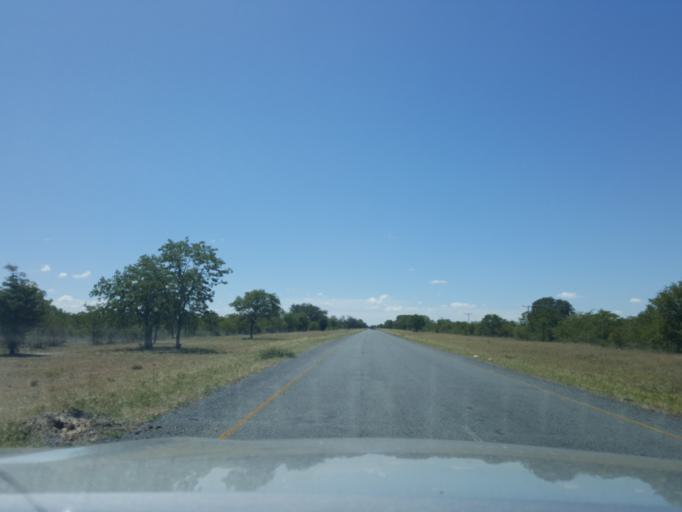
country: BW
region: Central
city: Gweta
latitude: -20.1797
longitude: 25.3246
